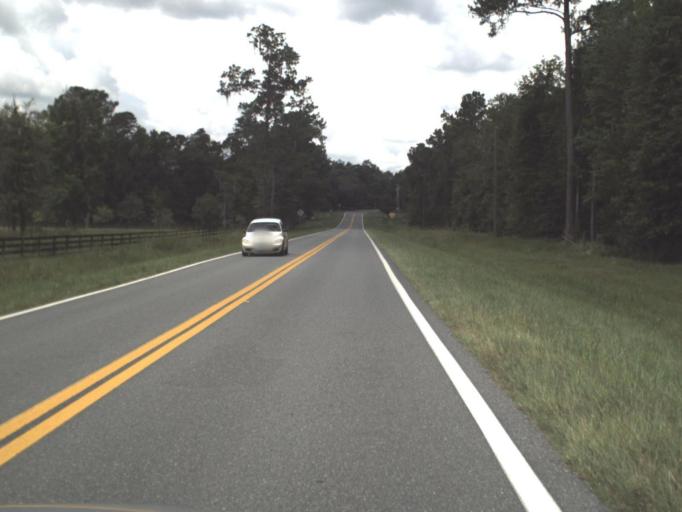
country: US
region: Florida
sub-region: Union County
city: Lake Butler
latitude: 29.9318
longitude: -82.4178
